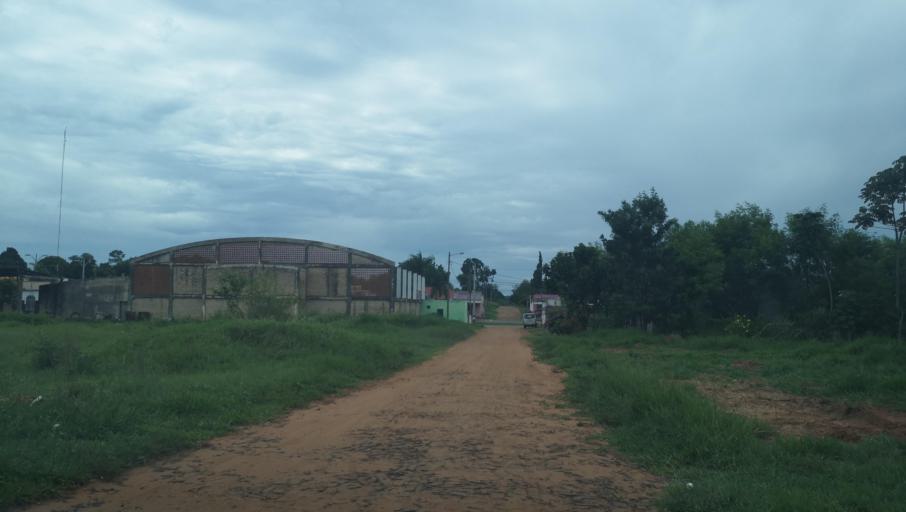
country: PY
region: San Pedro
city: Capiibary
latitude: -24.7349
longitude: -56.0205
